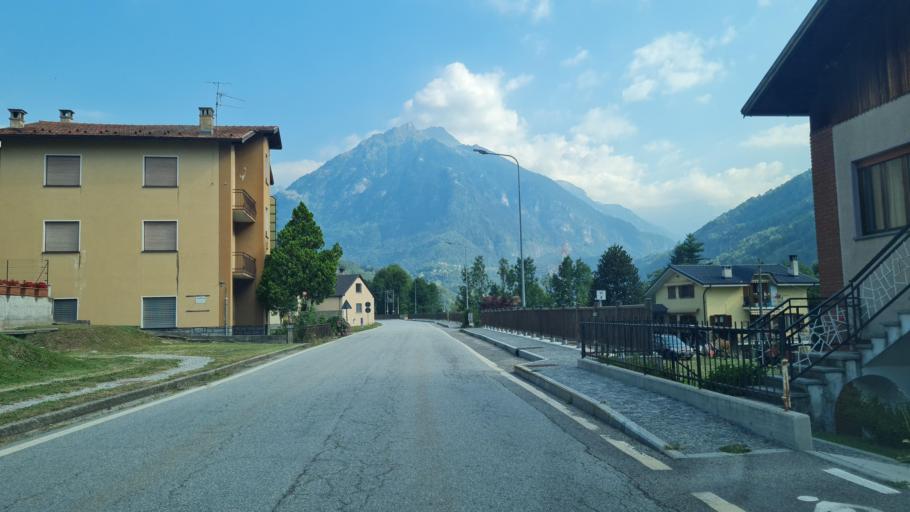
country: IT
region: Piedmont
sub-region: Provincia Verbano-Cusio-Ossola
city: Crodo
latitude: 46.2289
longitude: 8.3251
